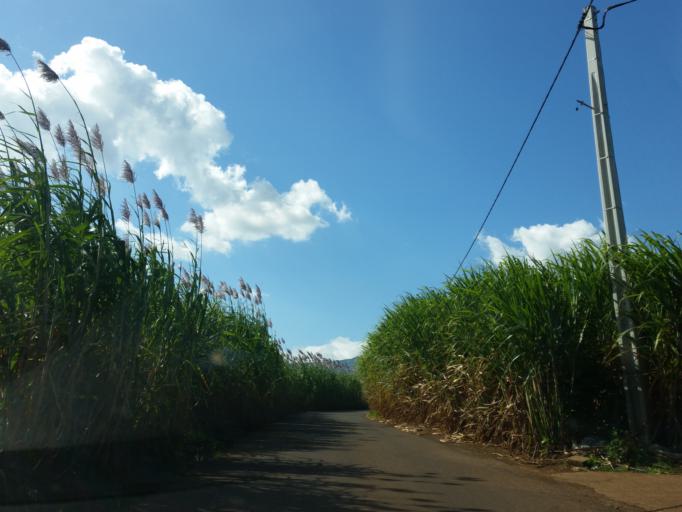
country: RE
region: Reunion
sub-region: Reunion
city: Saint-Pierre
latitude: -21.3167
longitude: 55.5057
